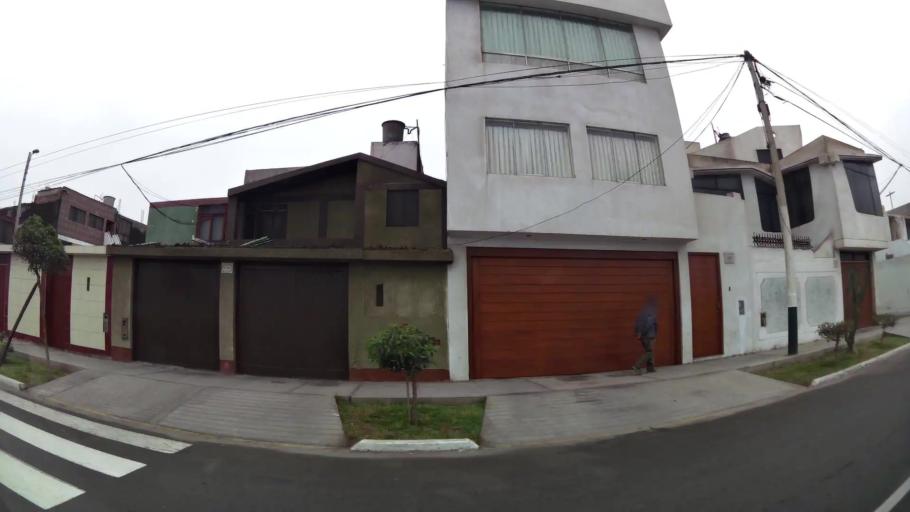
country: PE
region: Callao
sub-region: Callao
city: Callao
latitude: -12.0781
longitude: -77.1122
